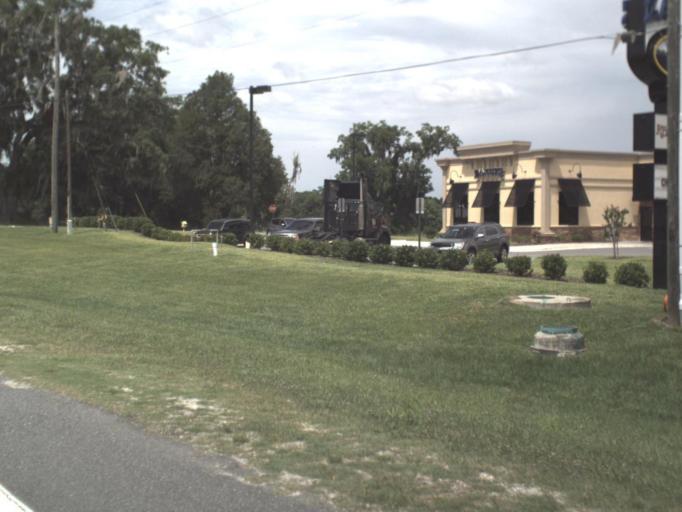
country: US
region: Florida
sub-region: Suwannee County
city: Live Oak
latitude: 30.3256
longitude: -82.9662
